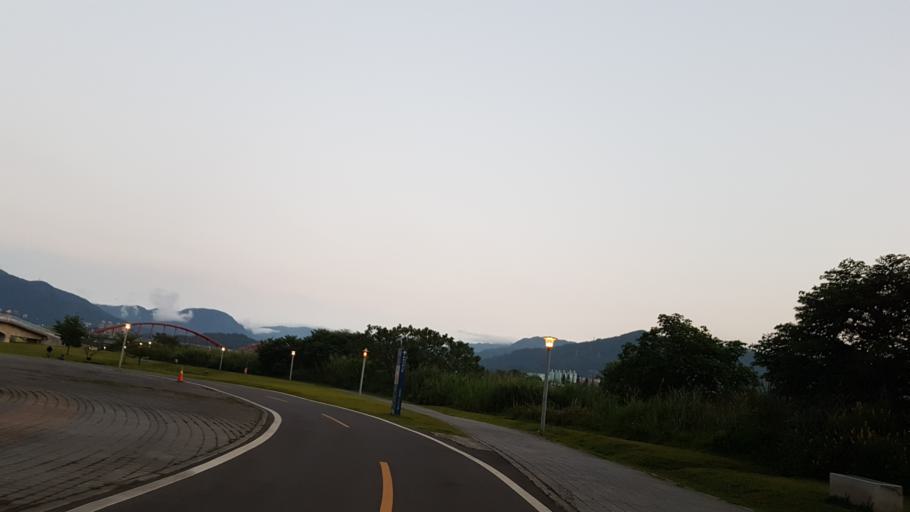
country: TW
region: Taipei
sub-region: Taipei
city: Banqiao
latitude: 24.9784
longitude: 121.5224
